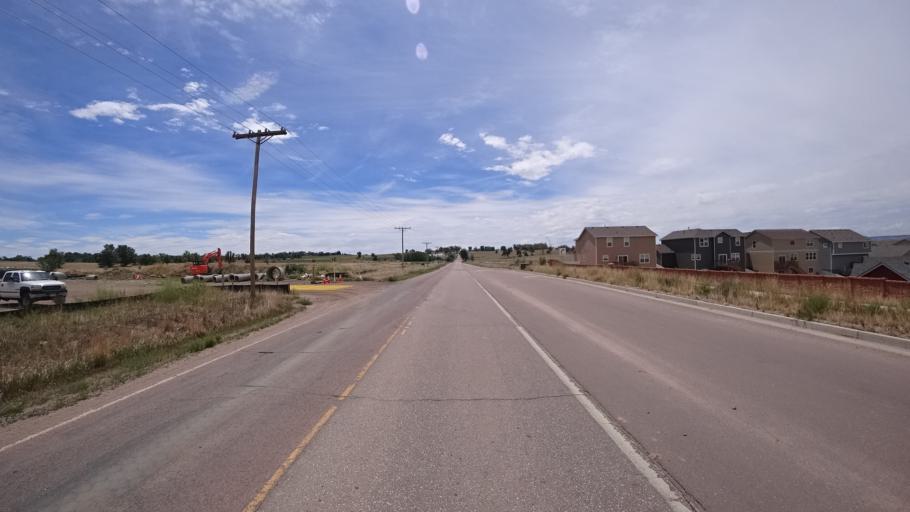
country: US
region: Colorado
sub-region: El Paso County
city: Fountain
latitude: 38.6909
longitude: -104.6736
